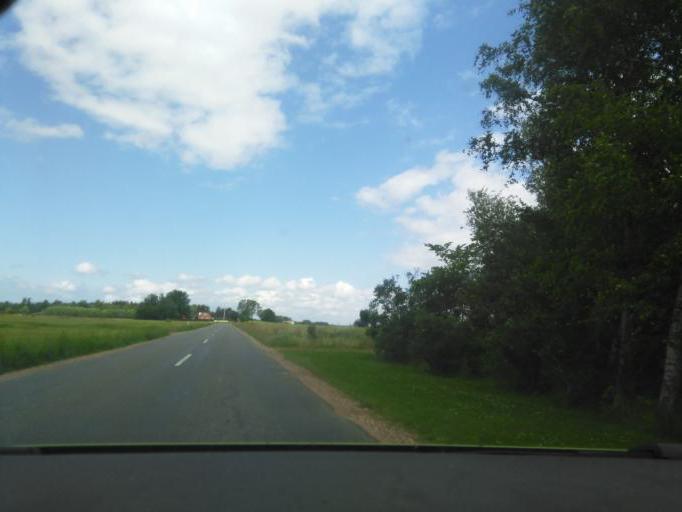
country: DK
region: Zealand
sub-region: Kalundborg Kommune
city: Gorlev
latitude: 55.5415
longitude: 11.1691
